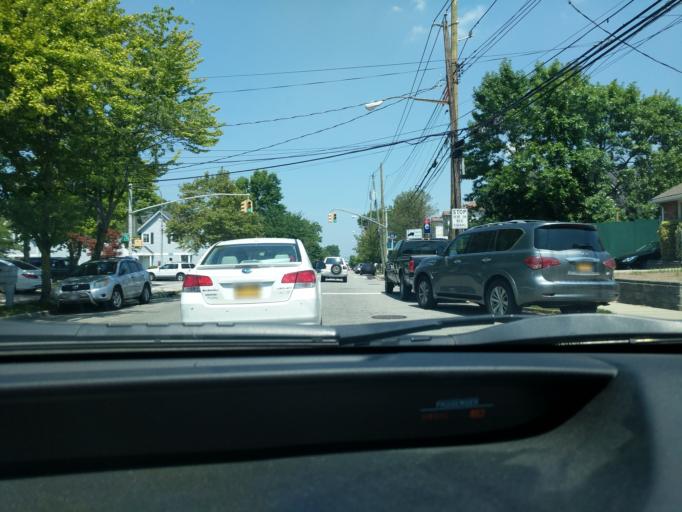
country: US
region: New Jersey
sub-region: Middlesex County
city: Carteret
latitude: 40.5461
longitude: -74.2097
